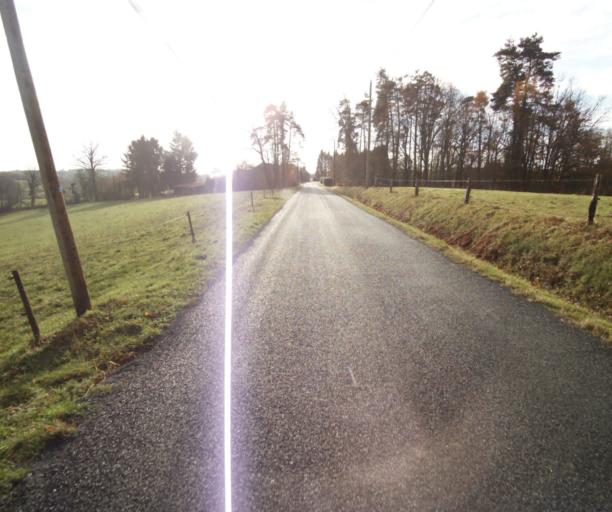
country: FR
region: Limousin
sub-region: Departement de la Correze
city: Sainte-Fereole
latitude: 45.2707
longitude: 1.6029
